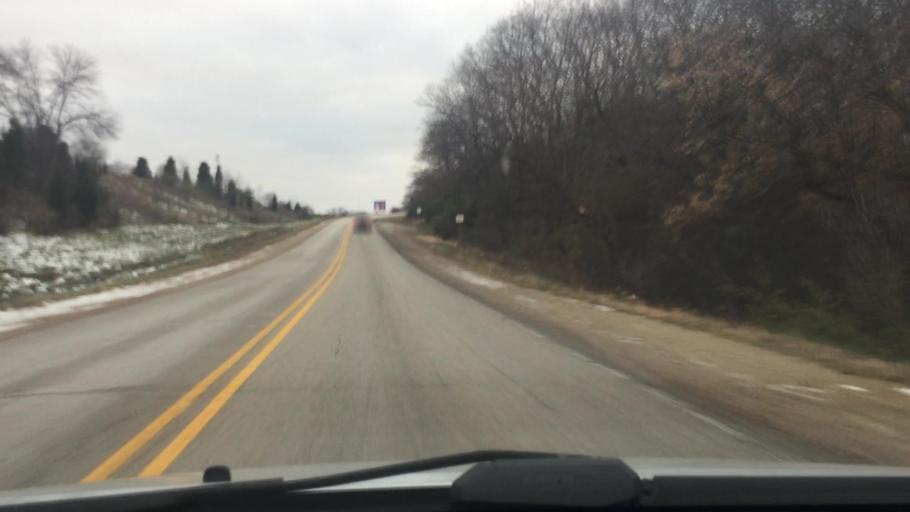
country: US
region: Wisconsin
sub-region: Waukesha County
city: Wales
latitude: 43.0498
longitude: -88.3499
